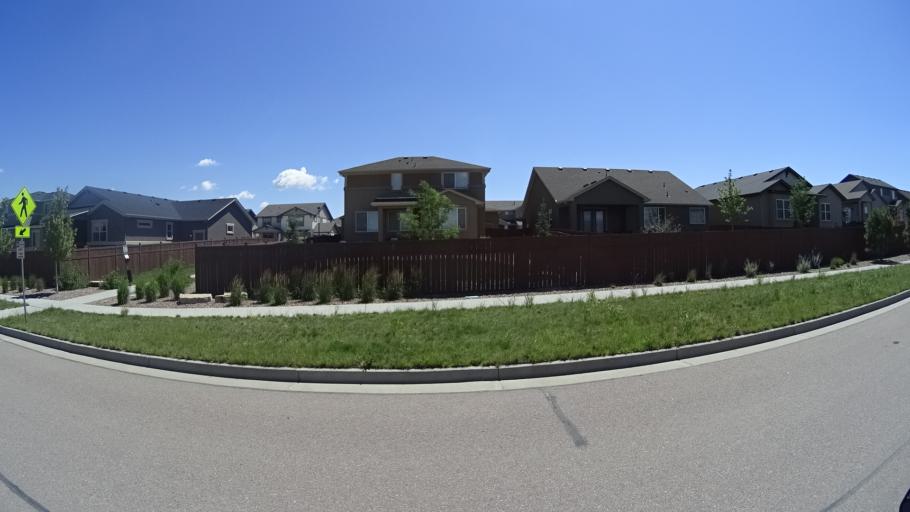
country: US
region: Colorado
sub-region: El Paso County
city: Black Forest
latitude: 38.9911
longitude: -104.7604
